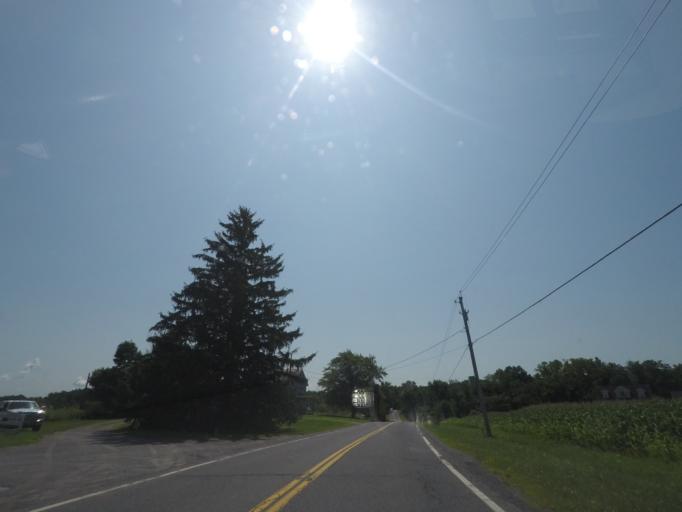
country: US
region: New York
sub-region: Saratoga County
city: Mechanicville
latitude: 42.8582
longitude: -73.7224
